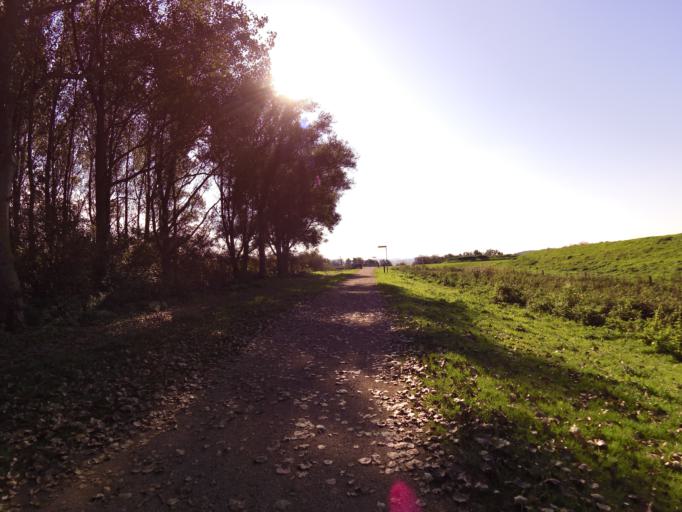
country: NL
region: South Holland
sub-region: Gemeente Vlaardingen
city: Vlaardingen
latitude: 51.9276
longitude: 4.3109
